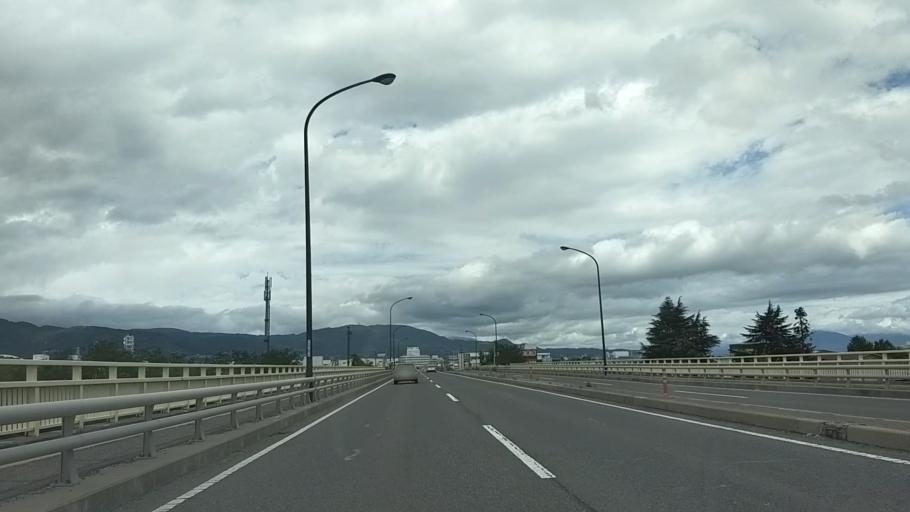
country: JP
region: Nagano
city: Nagano-shi
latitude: 36.6203
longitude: 138.1990
